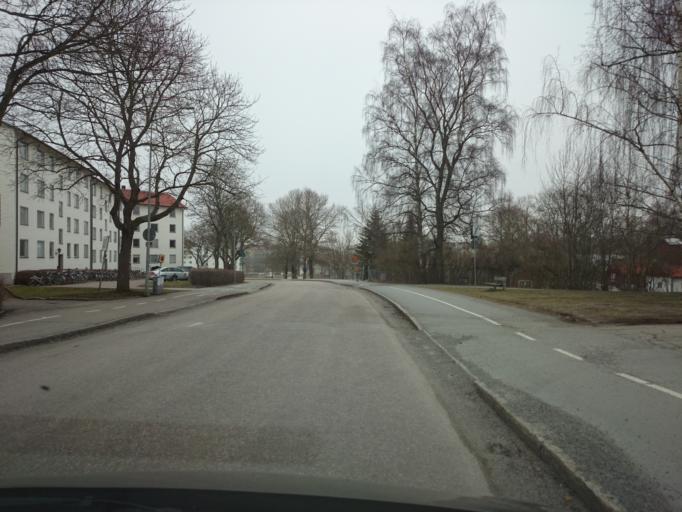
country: SE
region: Uppsala
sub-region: Uppsala Kommun
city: Uppsala
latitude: 59.8570
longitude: 17.6194
